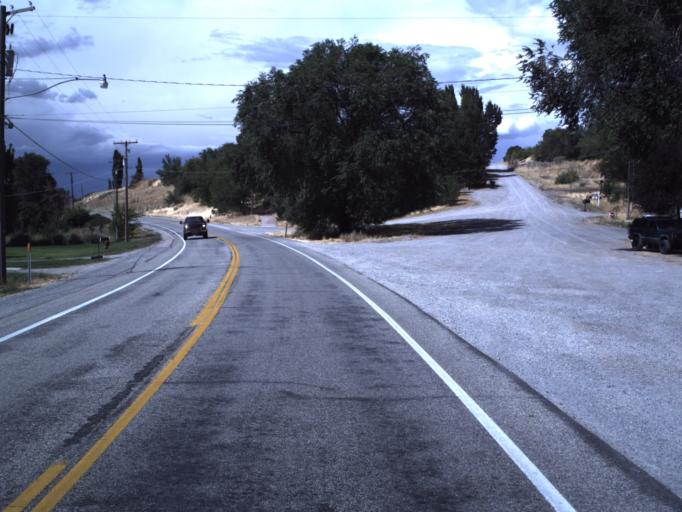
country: US
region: Utah
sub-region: Box Elder County
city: Elwood
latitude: 41.7102
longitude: -112.0903
